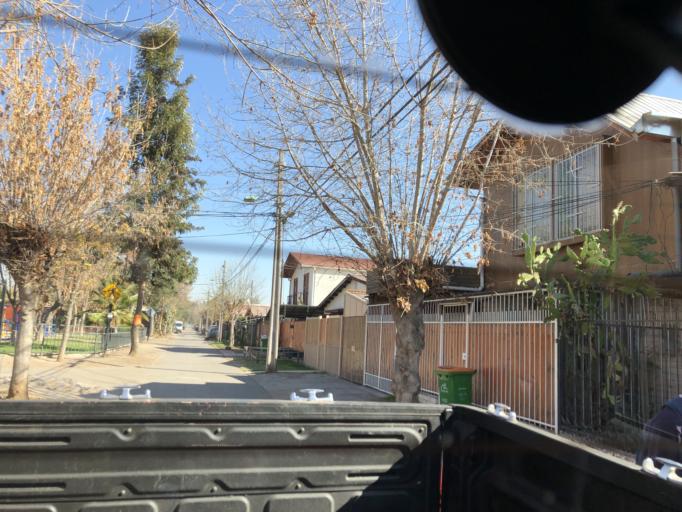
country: CL
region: Santiago Metropolitan
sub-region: Provincia de Cordillera
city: Puente Alto
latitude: -33.5688
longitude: -70.5750
